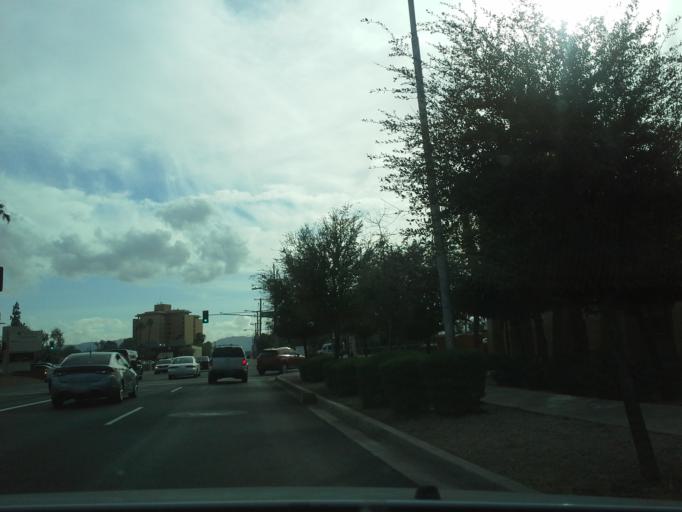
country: US
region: Arizona
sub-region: Maricopa County
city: Phoenix
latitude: 33.4374
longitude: -112.0826
